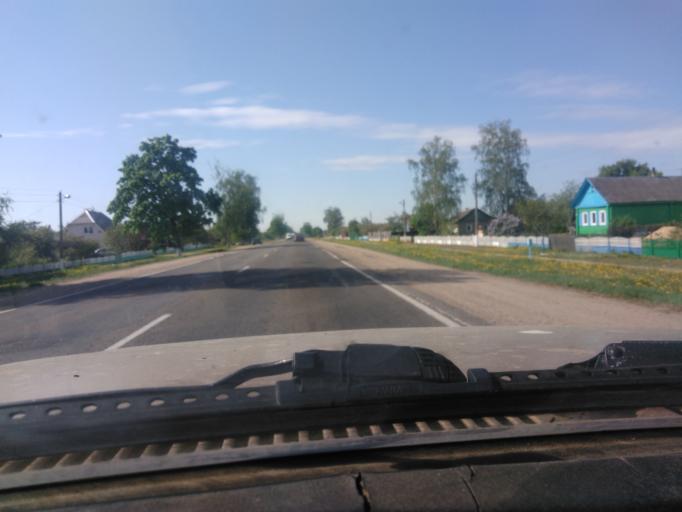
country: BY
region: Mogilev
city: Buynichy
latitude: 53.8386
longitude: 30.2475
